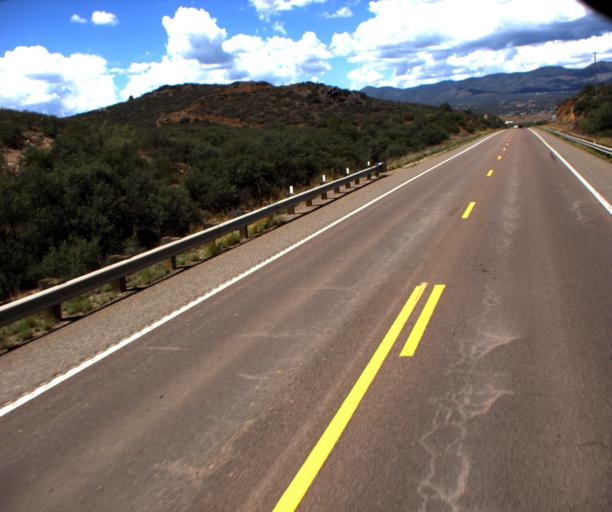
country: US
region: Arizona
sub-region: Yavapai County
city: Dewey-Humboldt
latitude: 34.5403
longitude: -112.1982
